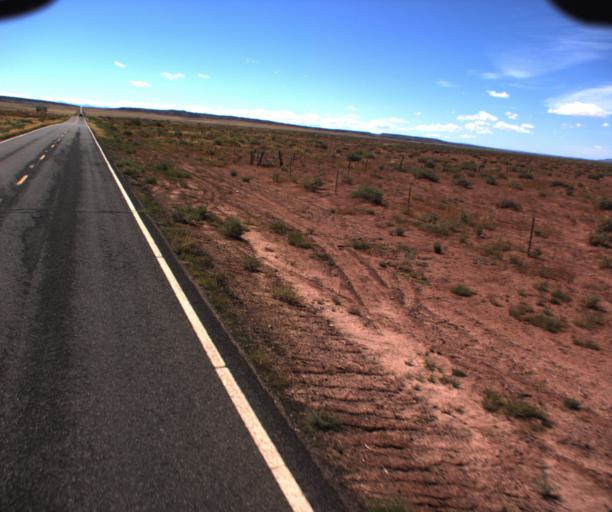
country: US
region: Arizona
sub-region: Apache County
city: Saint Johns
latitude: 34.7003
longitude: -109.2713
